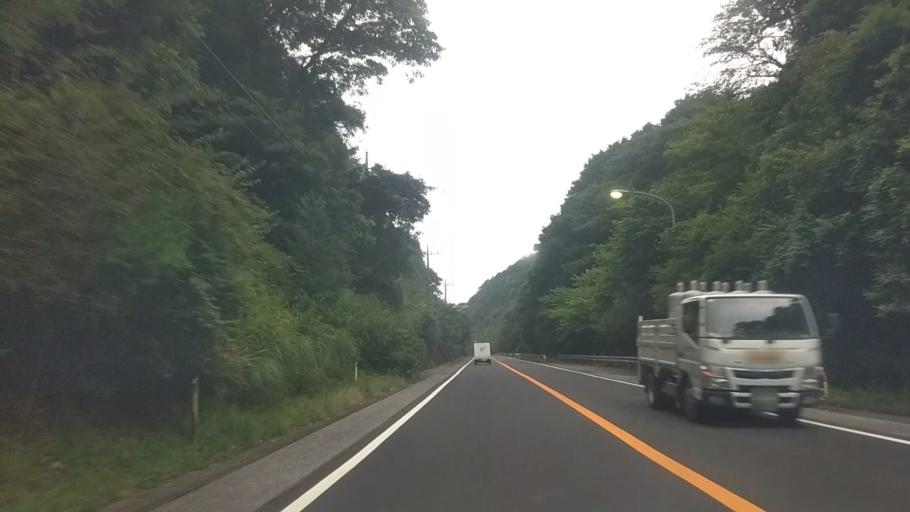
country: JP
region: Chiba
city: Kawaguchi
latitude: 35.1694
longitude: 140.0598
